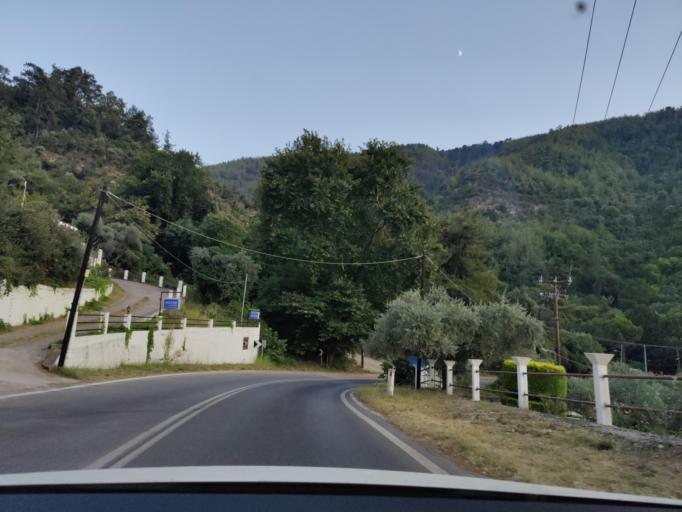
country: GR
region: East Macedonia and Thrace
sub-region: Nomos Kavalas
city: Potamia
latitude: 40.7064
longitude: 24.7634
